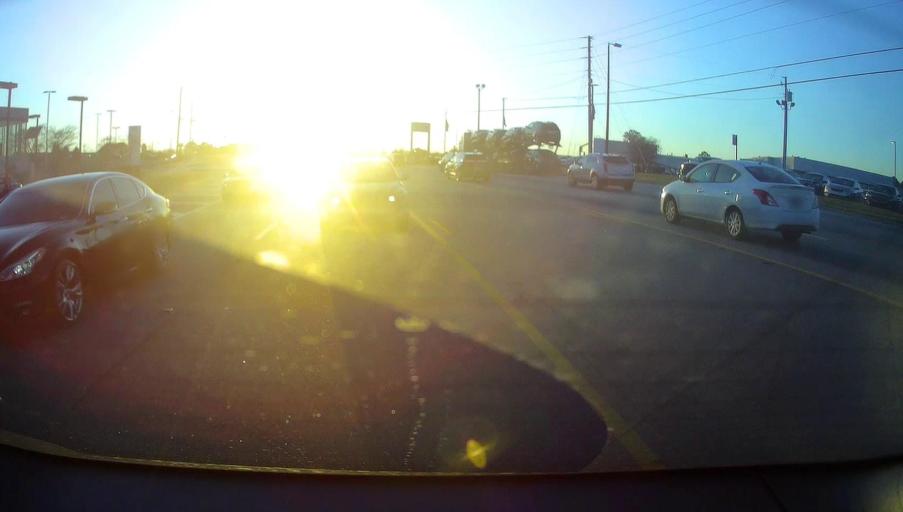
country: US
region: Georgia
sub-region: Fulton County
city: Union City
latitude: 33.5678
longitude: -84.5285
